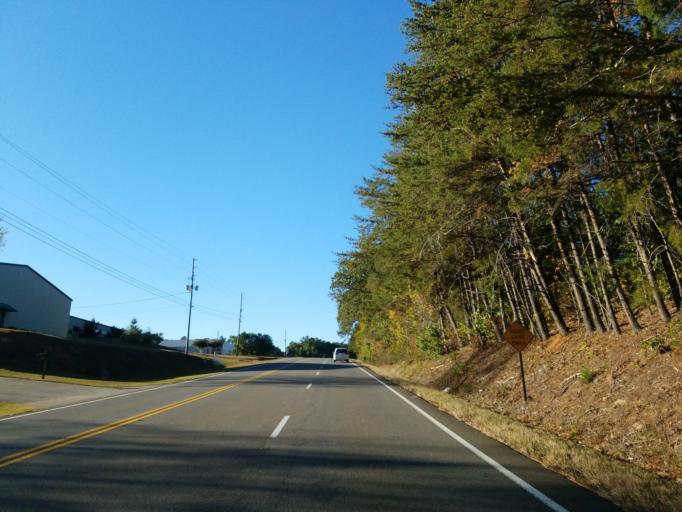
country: US
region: Georgia
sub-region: Pickens County
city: Nelson
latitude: 34.3908
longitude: -84.3779
